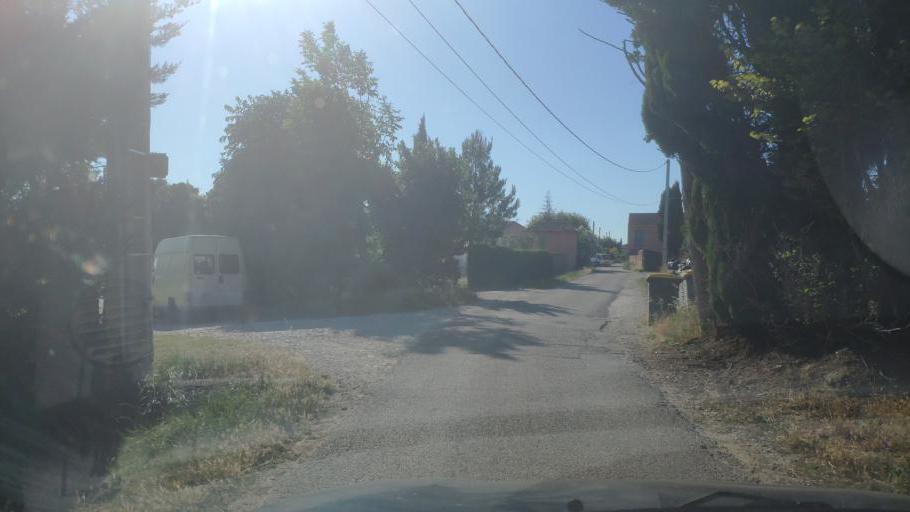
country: FR
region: Provence-Alpes-Cote d'Azur
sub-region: Departement du Vaucluse
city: Aubignan
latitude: 44.0892
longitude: 5.0387
